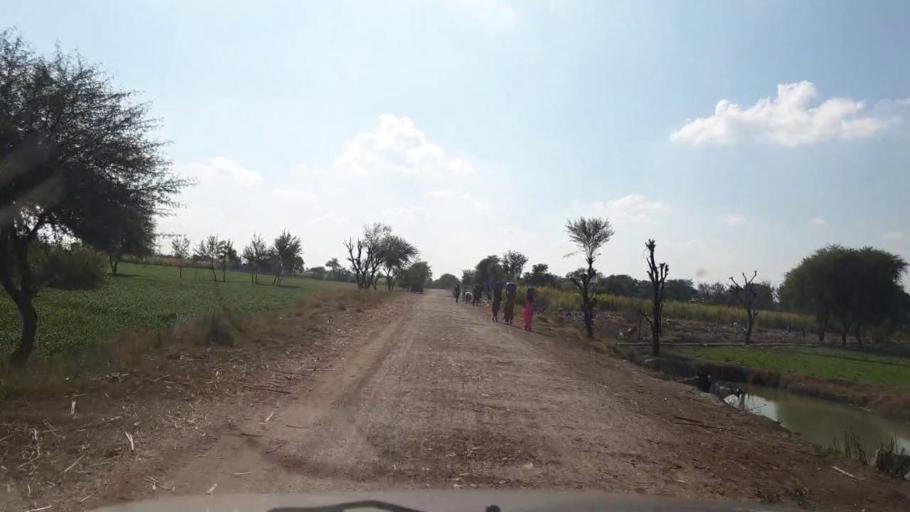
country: PK
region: Sindh
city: Sinjhoro
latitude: 26.0242
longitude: 68.7500
